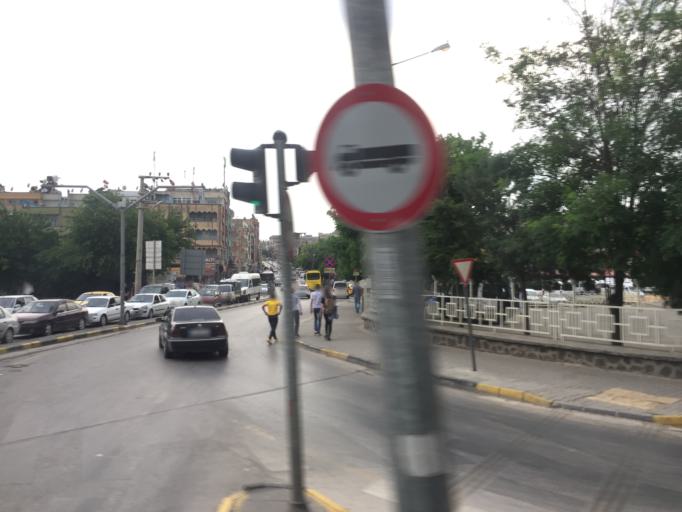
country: TR
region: Gaziantep
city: Gaziantep
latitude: 37.0675
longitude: 37.4142
